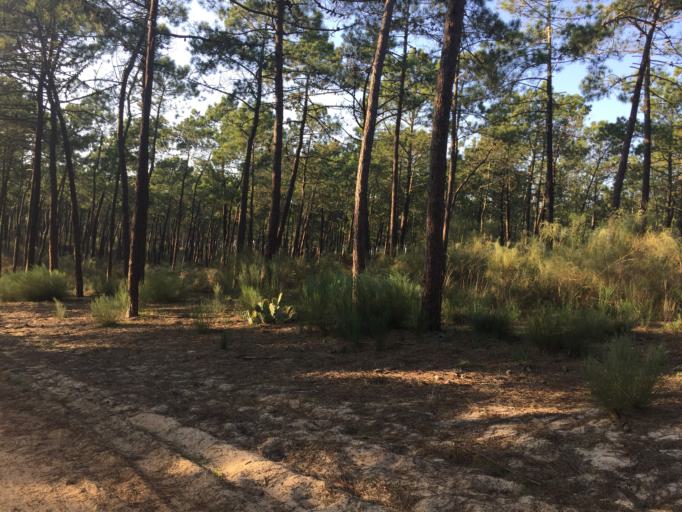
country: PT
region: Faro
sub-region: Vila Real de Santo Antonio
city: Vila Real de Santo Antonio
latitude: 37.1875
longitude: -7.4315
